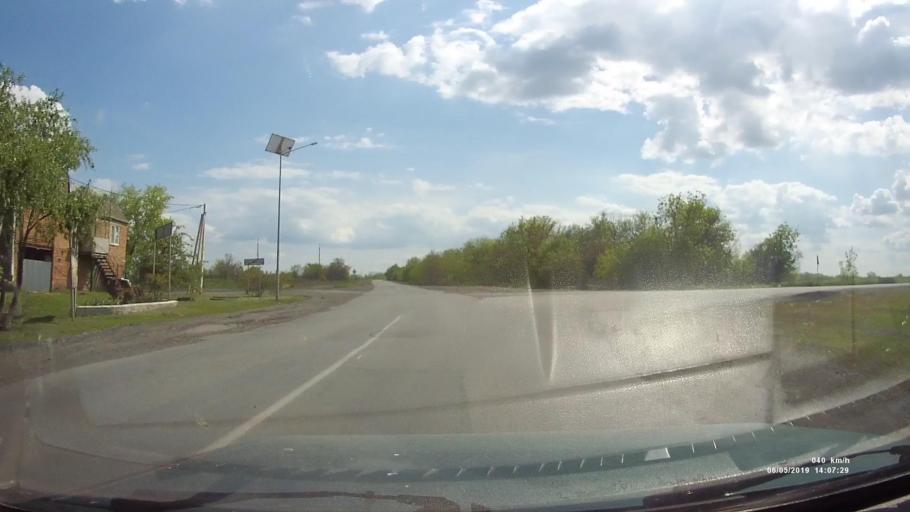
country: RU
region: Rostov
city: Shakhty
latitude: 47.6807
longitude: 40.3034
